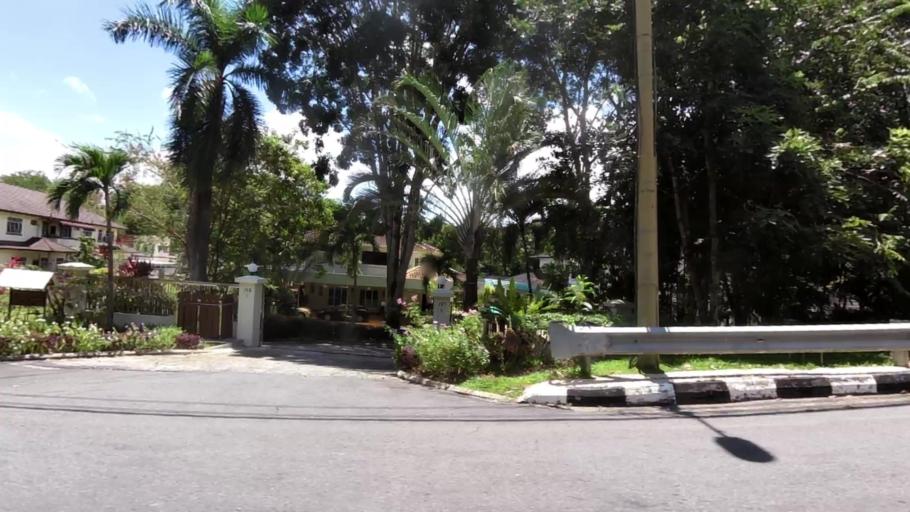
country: BN
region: Brunei and Muara
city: Bandar Seri Begawan
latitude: 4.9342
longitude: 114.9658
